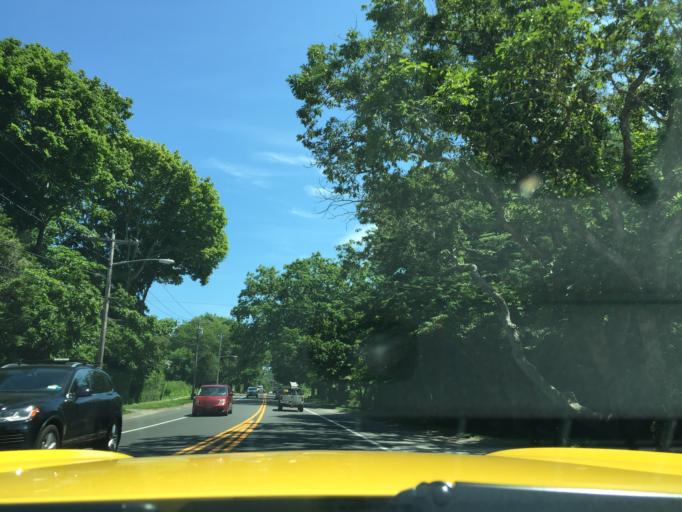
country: US
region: New York
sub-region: Suffolk County
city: Amagansett
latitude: 40.9706
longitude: -72.1550
